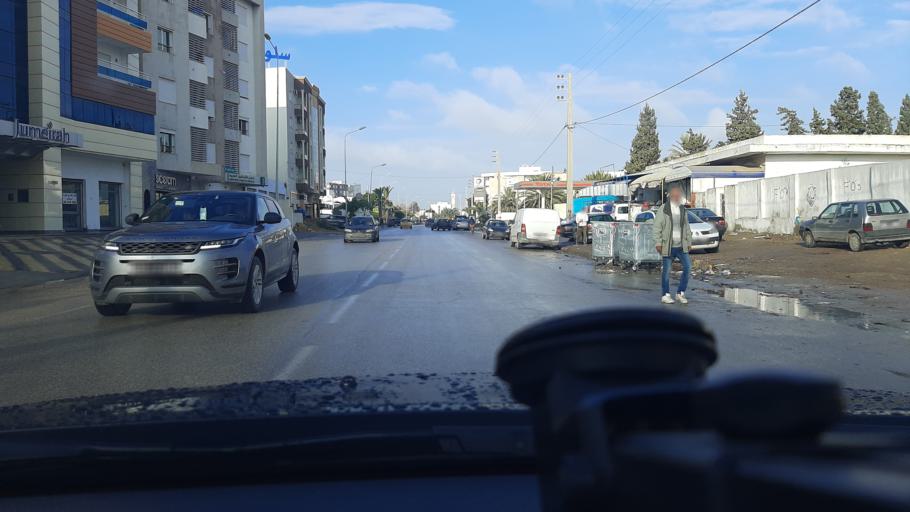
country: TN
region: Safaqis
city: Sfax
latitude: 34.7423
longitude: 10.7351
